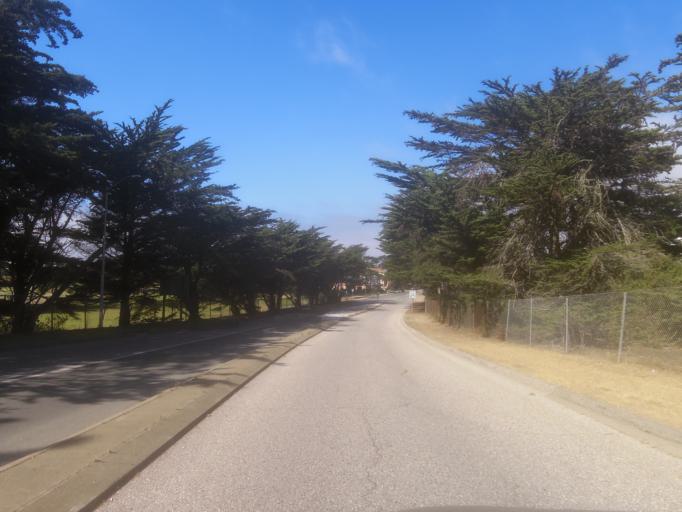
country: US
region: California
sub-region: San Mateo County
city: Pacifica
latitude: 37.6269
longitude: -122.4894
